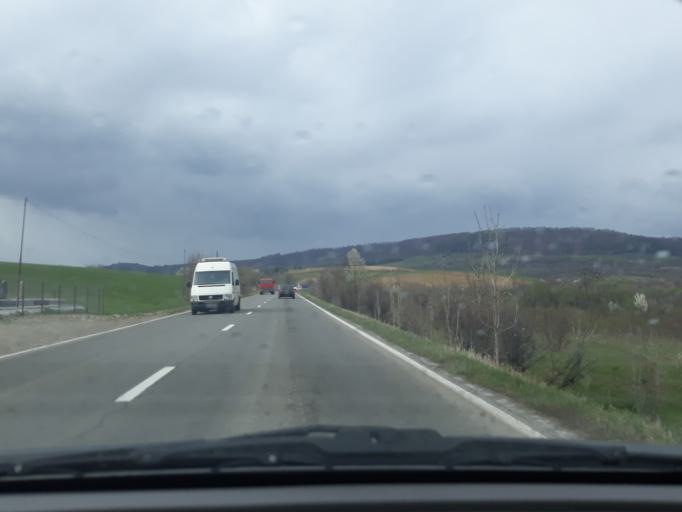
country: RO
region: Harghita
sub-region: Comuna Lupeni
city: Lupeni
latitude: 46.3915
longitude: 25.2151
